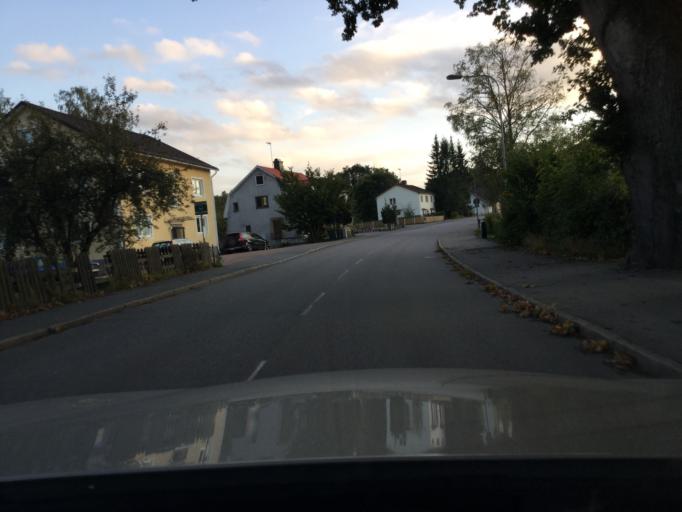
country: SE
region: Kronoberg
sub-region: Almhults Kommun
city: AElmhult
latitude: 56.6370
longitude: 14.2201
